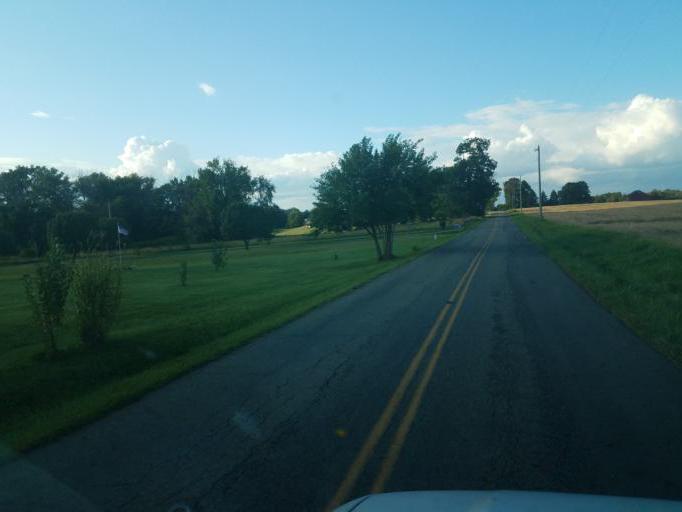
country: US
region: Ohio
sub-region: Knox County
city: Fredericktown
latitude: 40.4052
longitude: -82.5971
